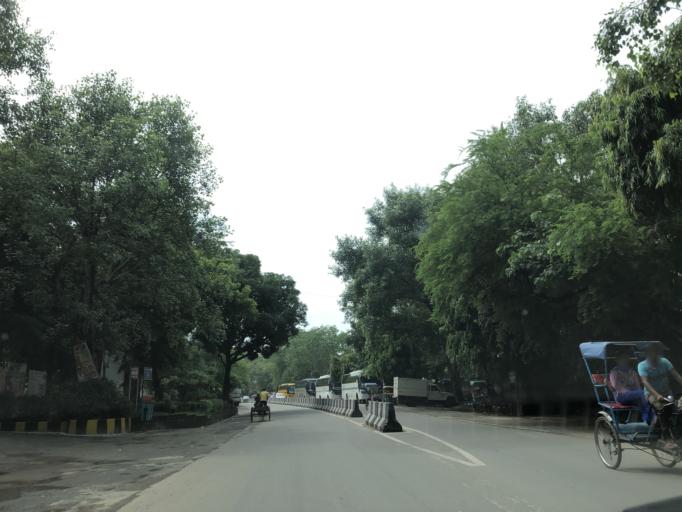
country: IN
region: NCT
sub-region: New Delhi
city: New Delhi
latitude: 28.5715
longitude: 77.2462
